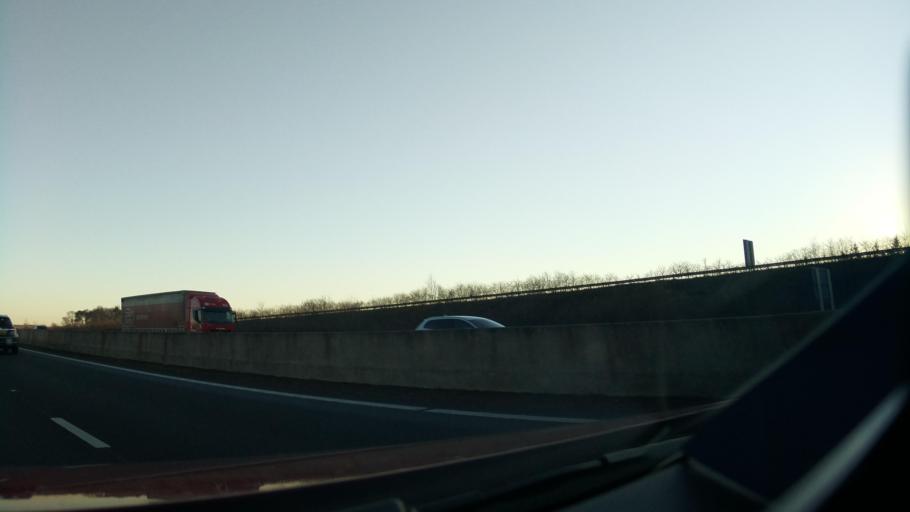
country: GB
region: England
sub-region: North Yorkshire
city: Bedale
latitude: 54.2826
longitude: -1.5392
